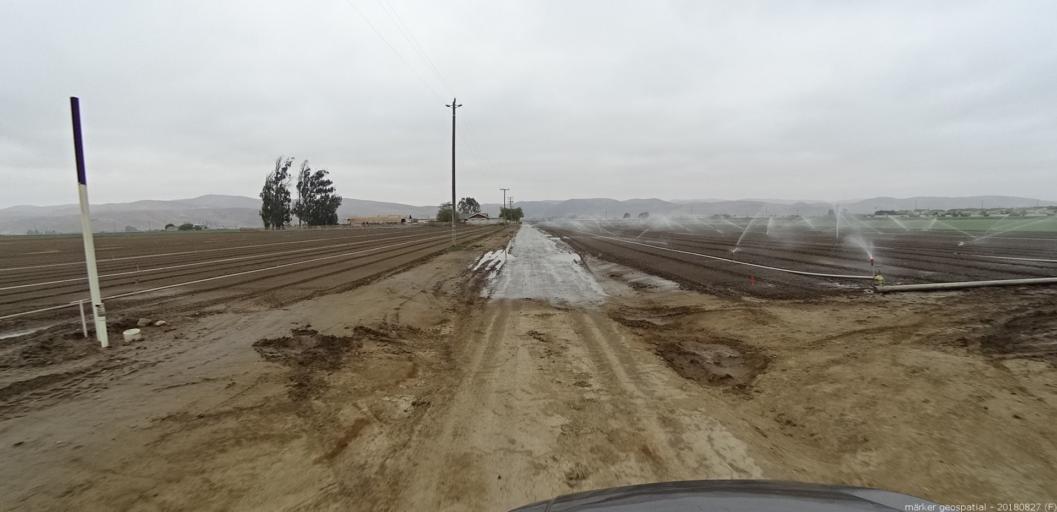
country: US
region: California
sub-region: Monterey County
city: Greenfield
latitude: 36.3359
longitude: -121.2401
